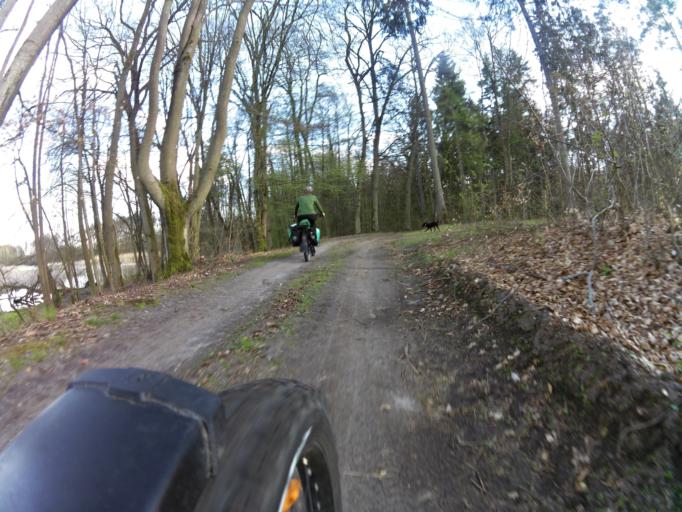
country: PL
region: West Pomeranian Voivodeship
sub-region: Powiat gryficki
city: Ploty
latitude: 53.7543
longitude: 15.2698
